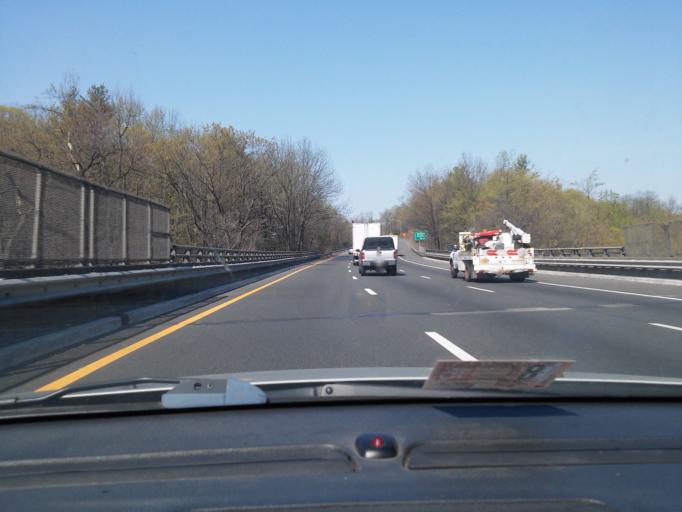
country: US
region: New Jersey
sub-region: Union County
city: Berkeley Heights
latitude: 40.6625
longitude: -74.4256
